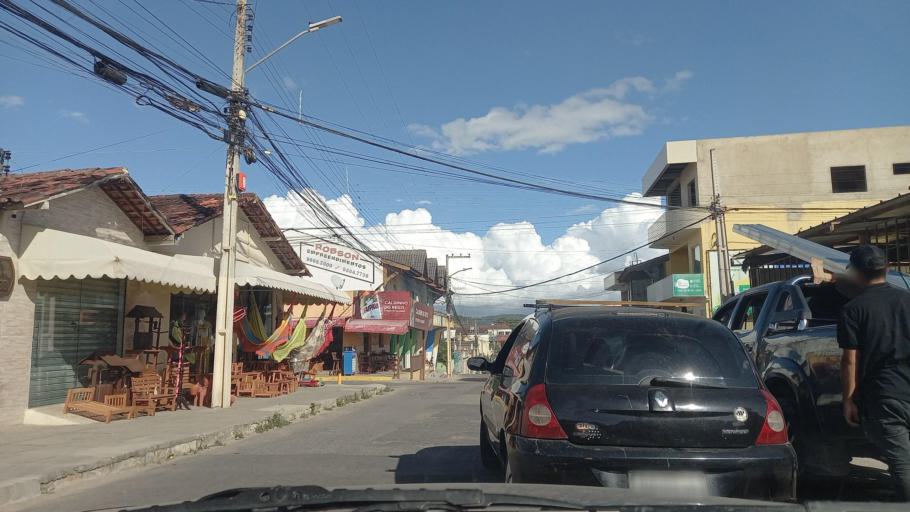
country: BR
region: Pernambuco
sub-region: Gravata
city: Gravata
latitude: -8.1974
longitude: -35.5635
